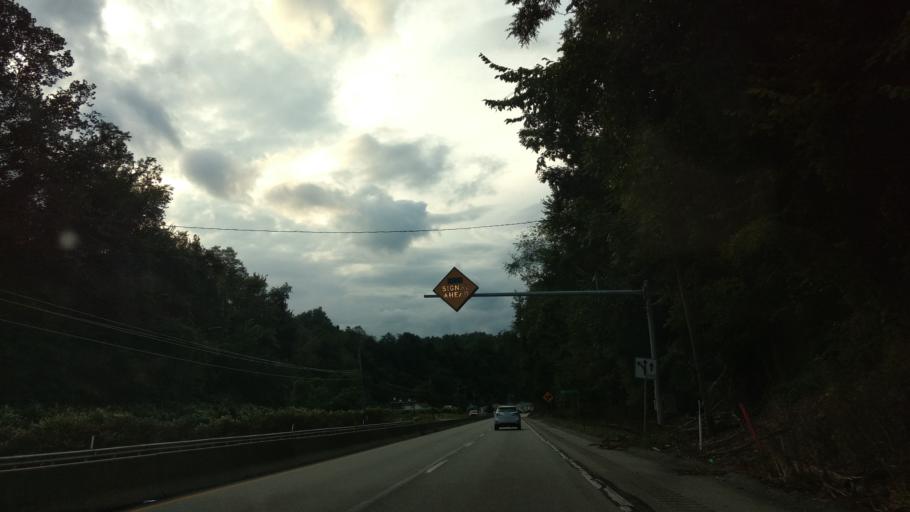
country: US
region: Pennsylvania
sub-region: Allegheny County
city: Elizabeth
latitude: 40.2470
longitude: -79.8746
